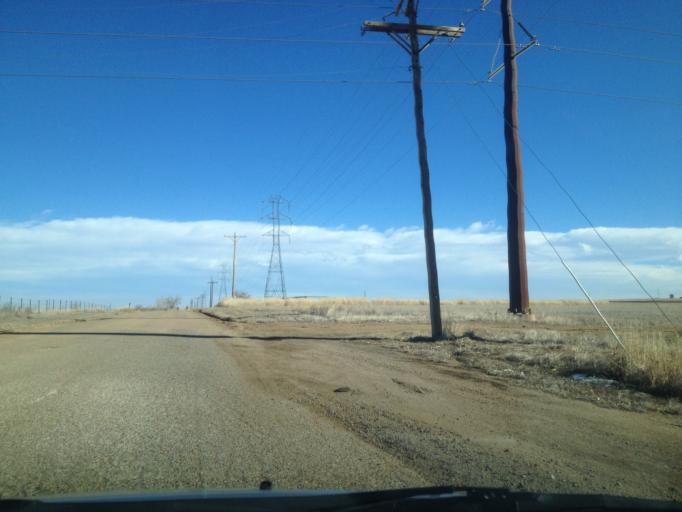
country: US
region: Colorado
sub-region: Weld County
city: Dacono
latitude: 40.0584
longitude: -104.9709
